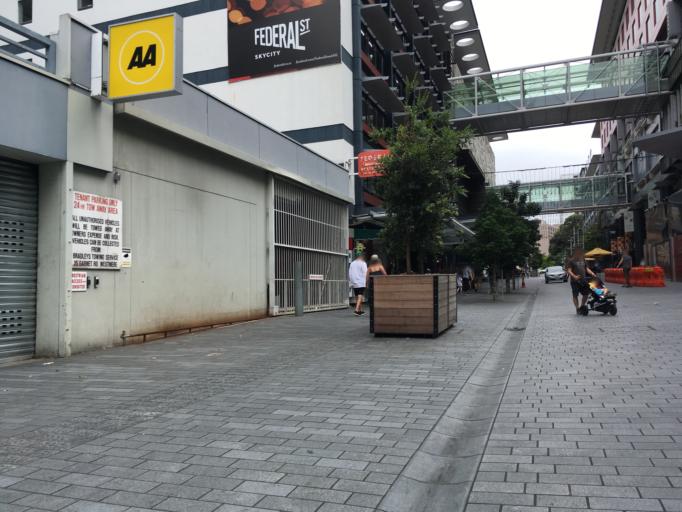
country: NZ
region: Auckland
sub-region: Auckland
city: Auckland
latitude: -36.8487
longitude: 174.7623
